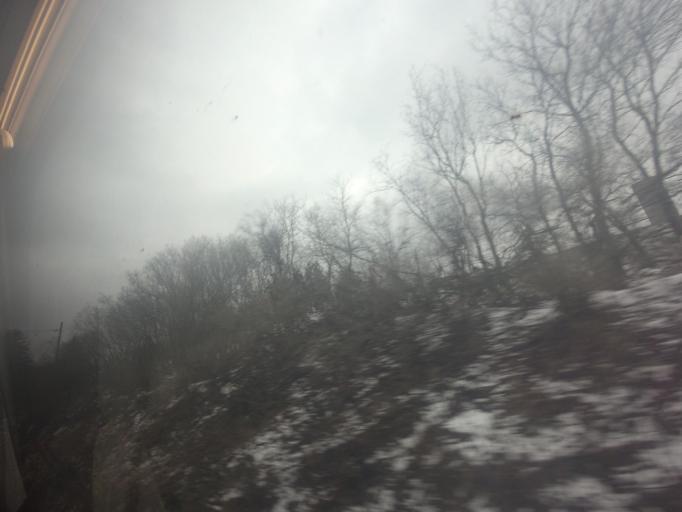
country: CA
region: Ontario
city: Cobourg
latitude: 43.9497
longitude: -78.2814
